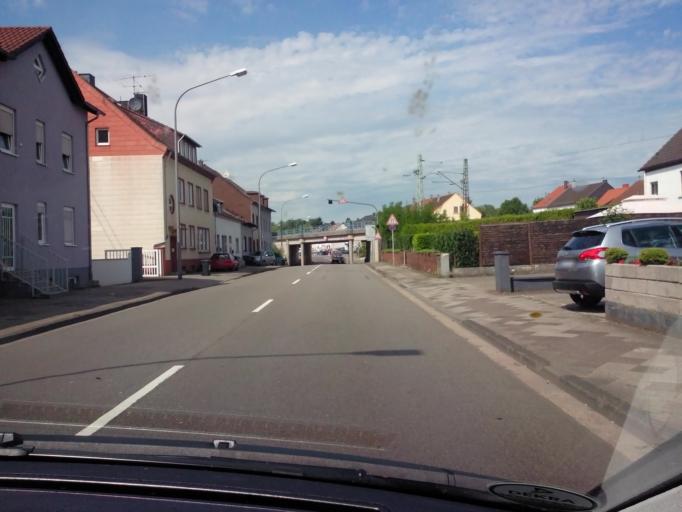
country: DE
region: Saarland
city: Saarlouis
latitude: 49.3321
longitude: 6.7442
